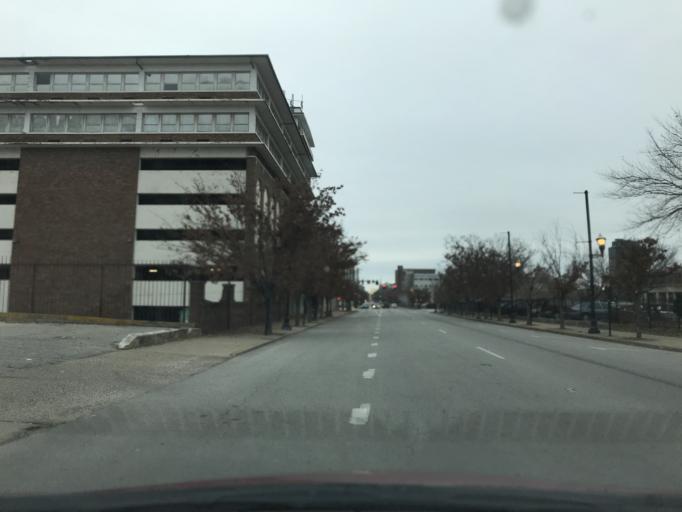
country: US
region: Kentucky
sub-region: Jefferson County
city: Louisville
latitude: 38.2446
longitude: -85.7554
